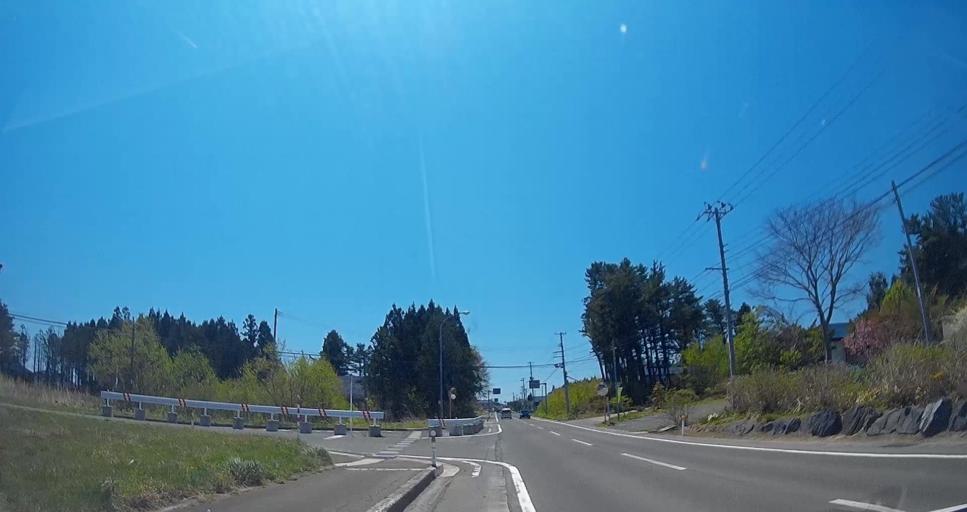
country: JP
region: Aomori
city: Mutsu
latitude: 41.0800
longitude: 141.3858
